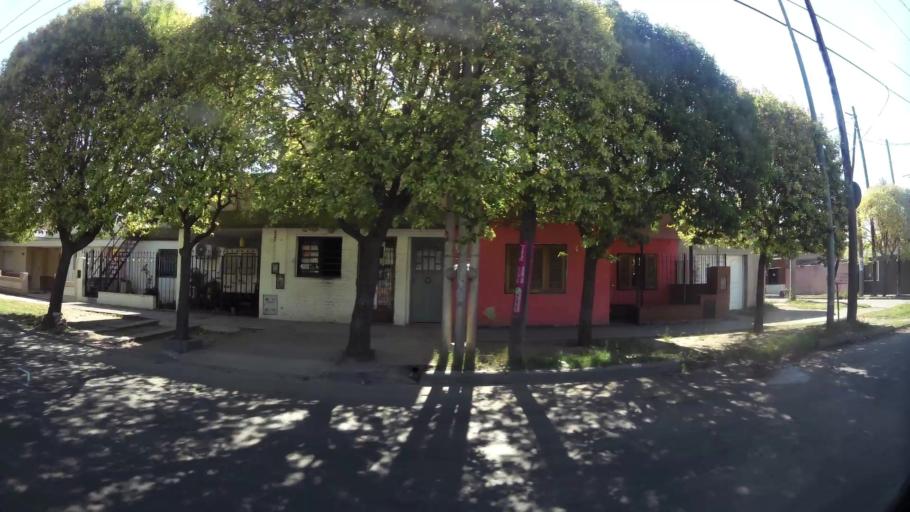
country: AR
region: Cordoba
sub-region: Departamento de Capital
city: Cordoba
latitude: -31.3648
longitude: -64.1839
